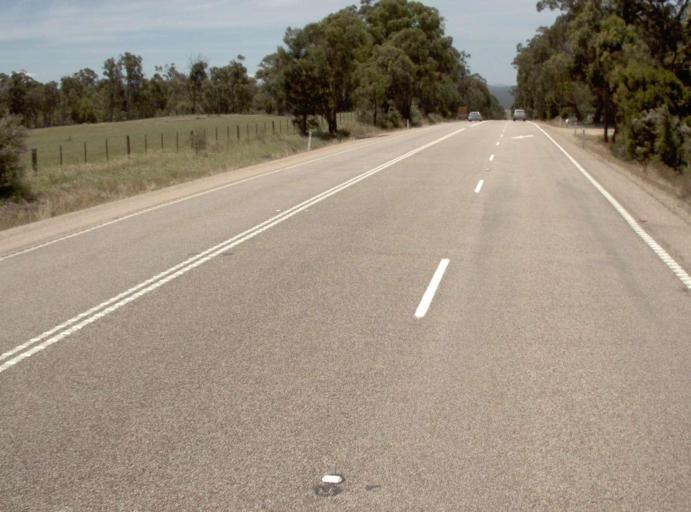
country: AU
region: Victoria
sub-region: East Gippsland
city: Bairnsdale
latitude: -37.7764
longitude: 147.6867
